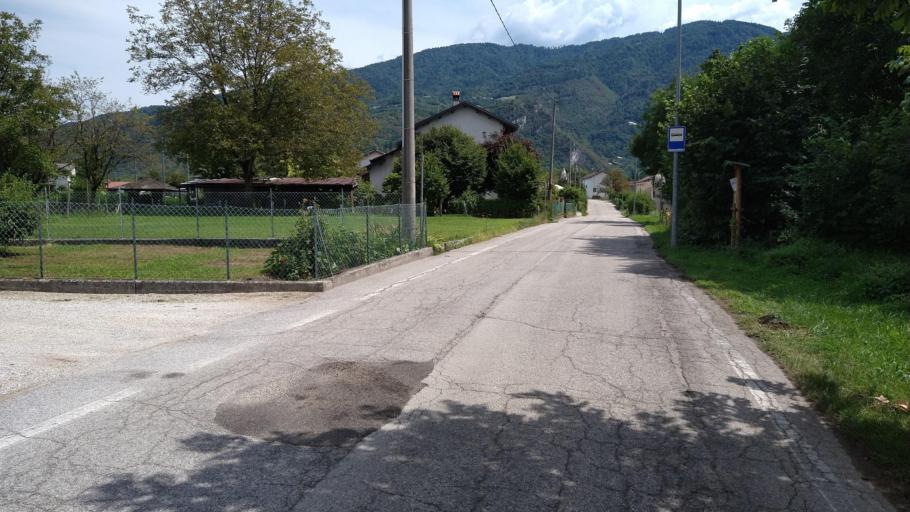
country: IT
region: Veneto
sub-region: Provincia di Belluno
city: Villabruna-Umin
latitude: 46.0115
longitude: 11.9625
